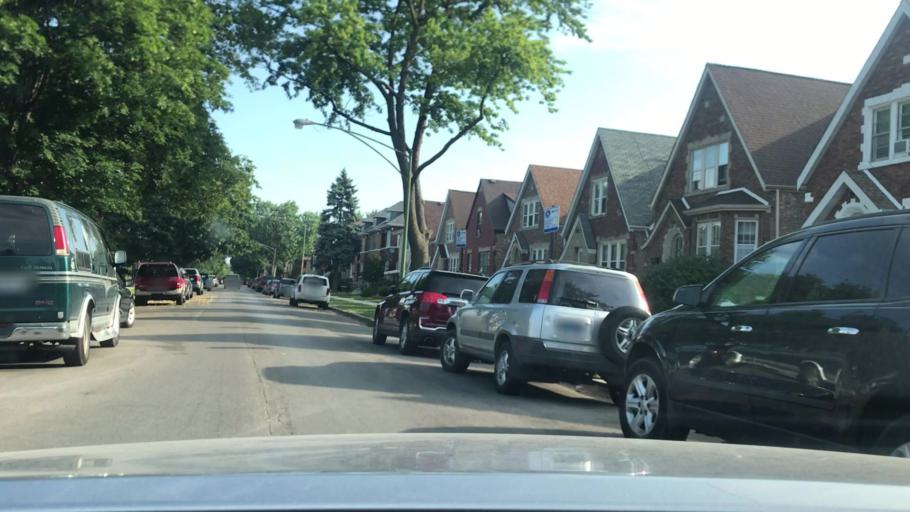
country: US
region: Illinois
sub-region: Cook County
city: Evergreen Park
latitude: 41.7610
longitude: -87.6929
